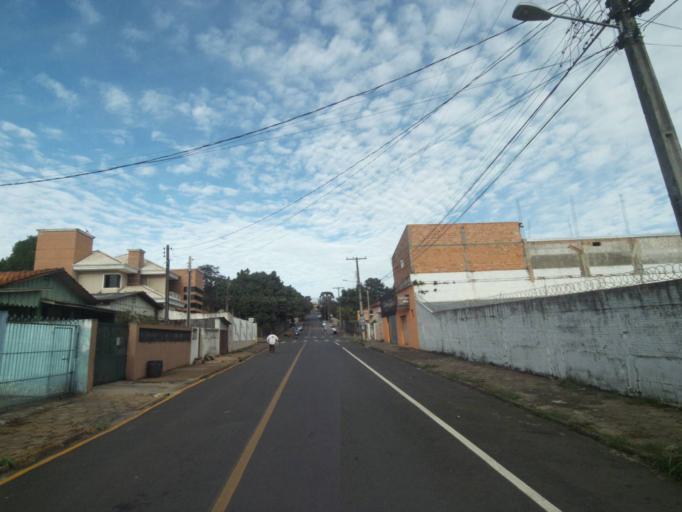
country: BR
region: Parana
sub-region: Telemaco Borba
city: Telemaco Borba
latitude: -24.3329
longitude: -50.6265
